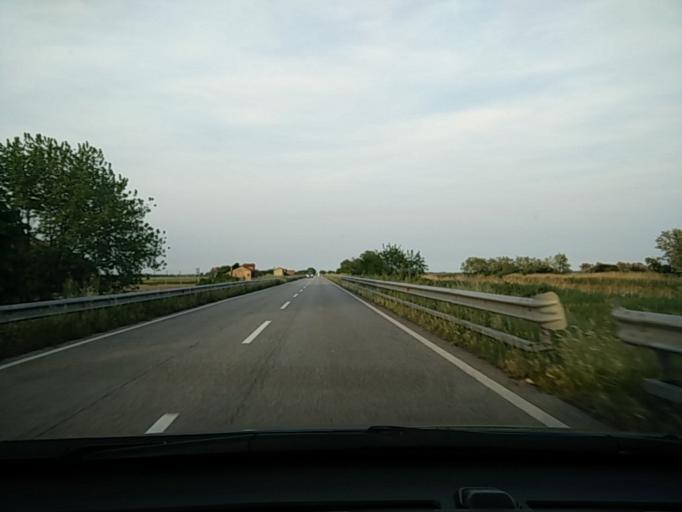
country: IT
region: Veneto
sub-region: Provincia di Venezia
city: Meolo
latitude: 45.5646
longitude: 12.4805
